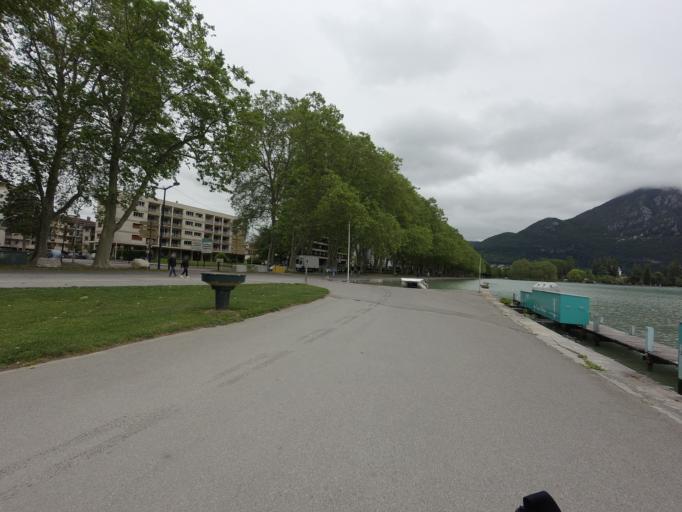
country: FR
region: Rhone-Alpes
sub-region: Departement de la Haute-Savoie
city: Annecy-le-Vieux
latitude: 45.9030
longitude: 6.1357
